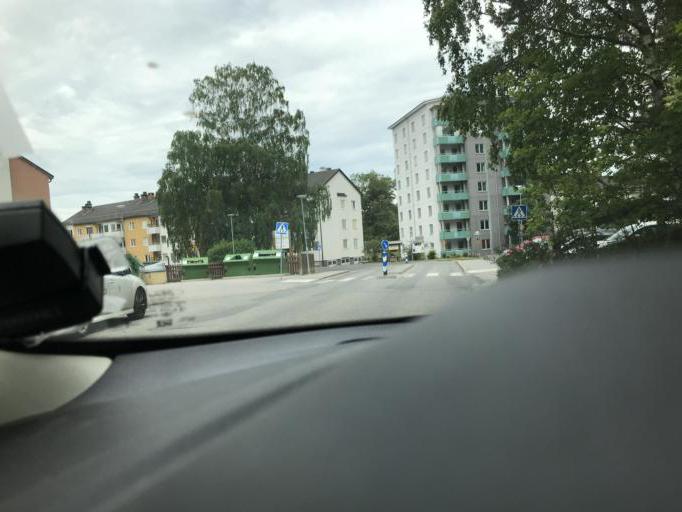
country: SE
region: Stockholm
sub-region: Botkyrka Kommun
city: Tumba
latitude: 59.1955
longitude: 17.8147
